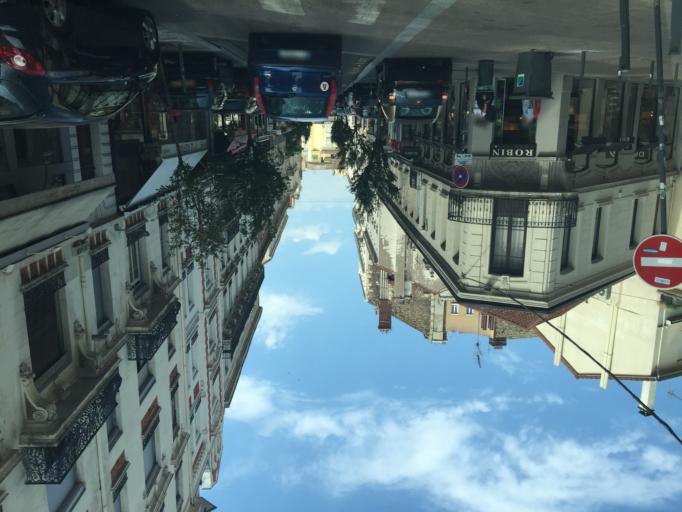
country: FR
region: Rhone-Alpes
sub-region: Departement de la Loire
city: Saint-Etienne
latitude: 45.4354
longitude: 4.3895
